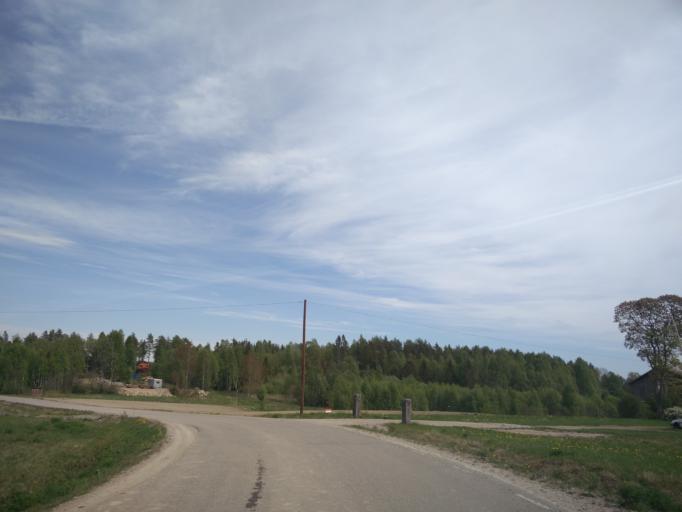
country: SE
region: Gaevleborg
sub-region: Hudiksvalls Kommun
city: Sorforsa
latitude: 61.7035
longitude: 16.9414
